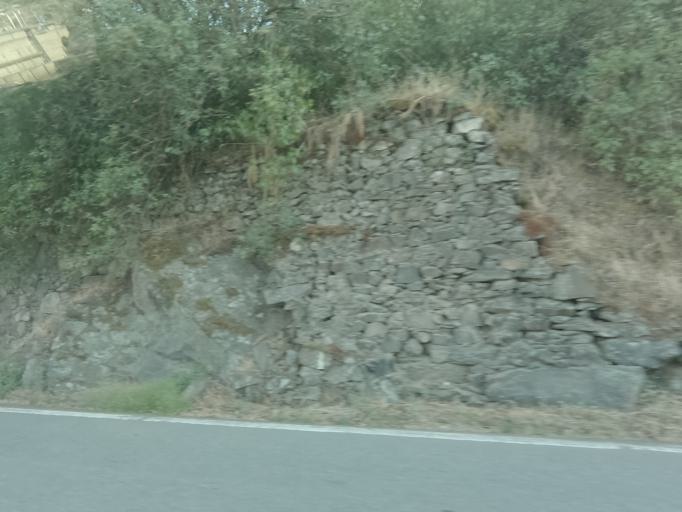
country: PT
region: Vila Real
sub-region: Peso da Regua
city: Peso da Regua
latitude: 41.1462
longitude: -7.7455
